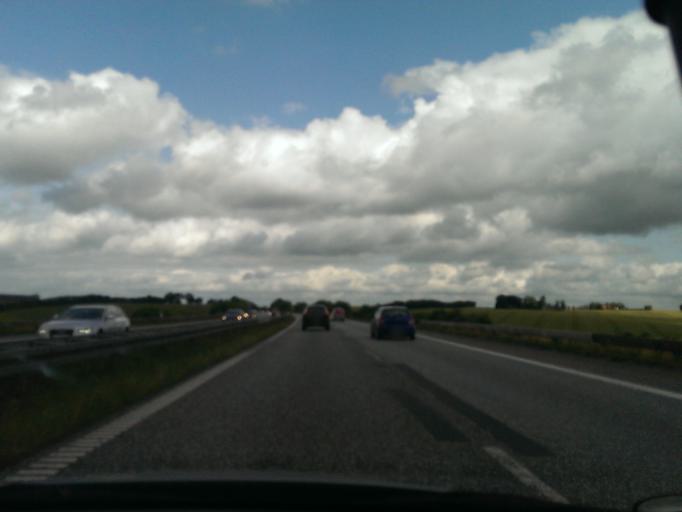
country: DK
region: North Denmark
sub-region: Mariagerfjord Kommune
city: Hobro
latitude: 56.5988
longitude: 9.7588
